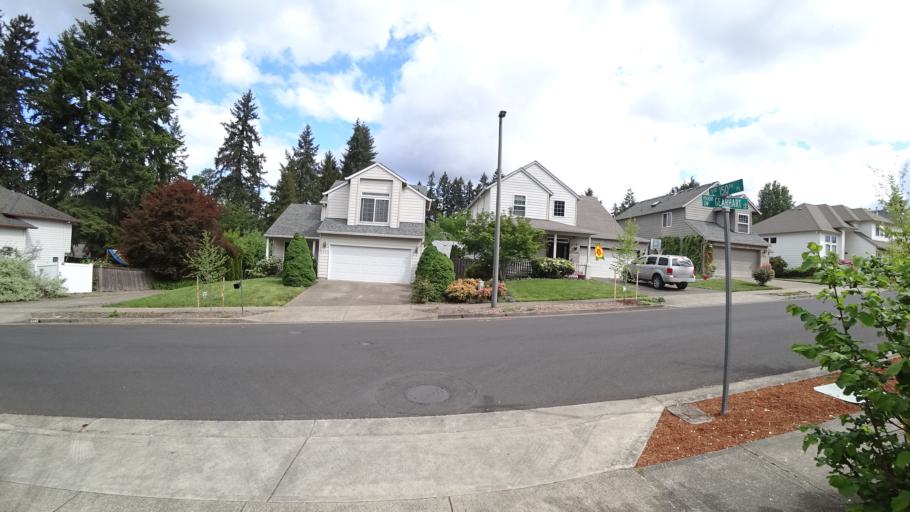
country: US
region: Oregon
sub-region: Washington County
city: Beaverton
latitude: 45.4645
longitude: -122.8335
